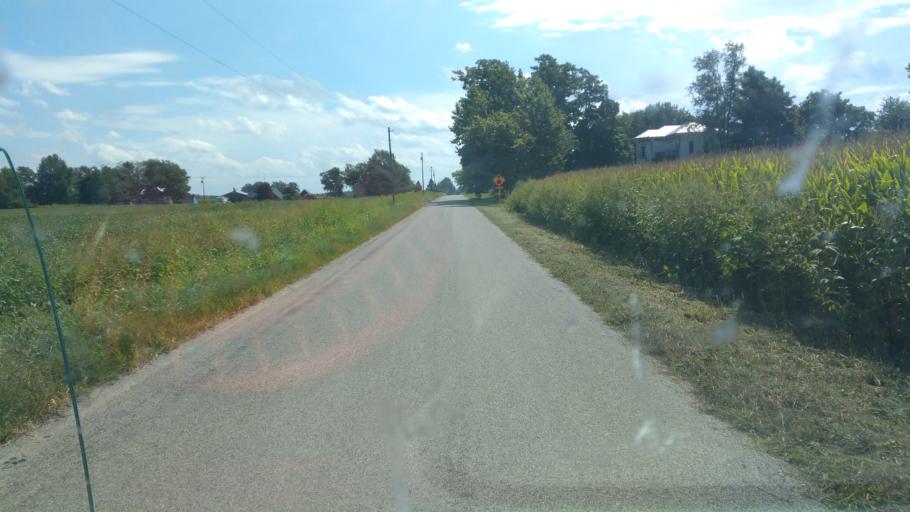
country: US
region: Ohio
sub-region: Union County
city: Richwood
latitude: 40.6025
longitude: -83.3430
